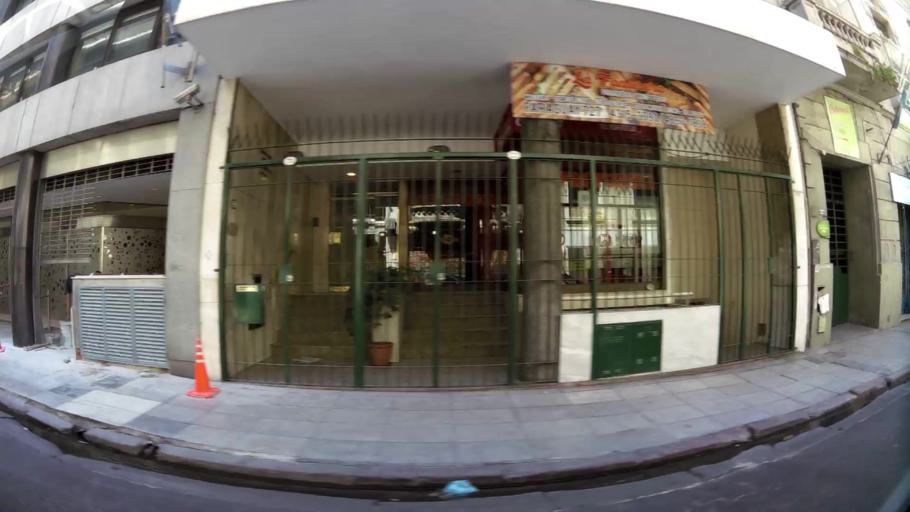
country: AR
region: Buenos Aires F.D.
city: Buenos Aires
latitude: -34.5977
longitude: -58.3776
